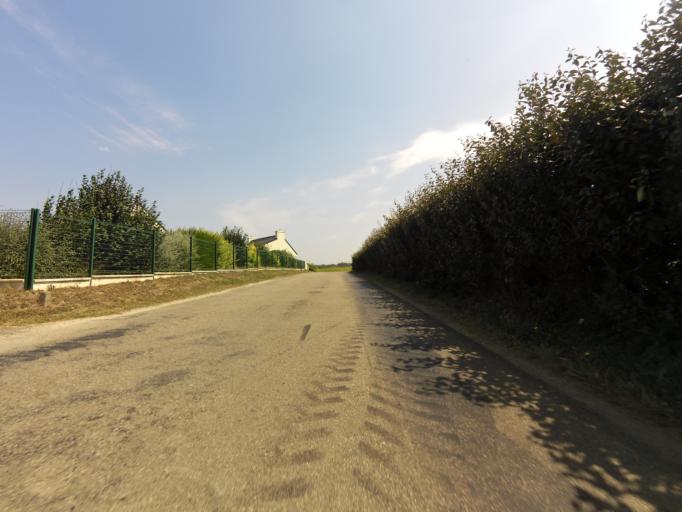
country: FR
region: Brittany
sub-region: Departement du Finistere
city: Pouldreuzic
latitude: 47.9138
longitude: -4.3570
